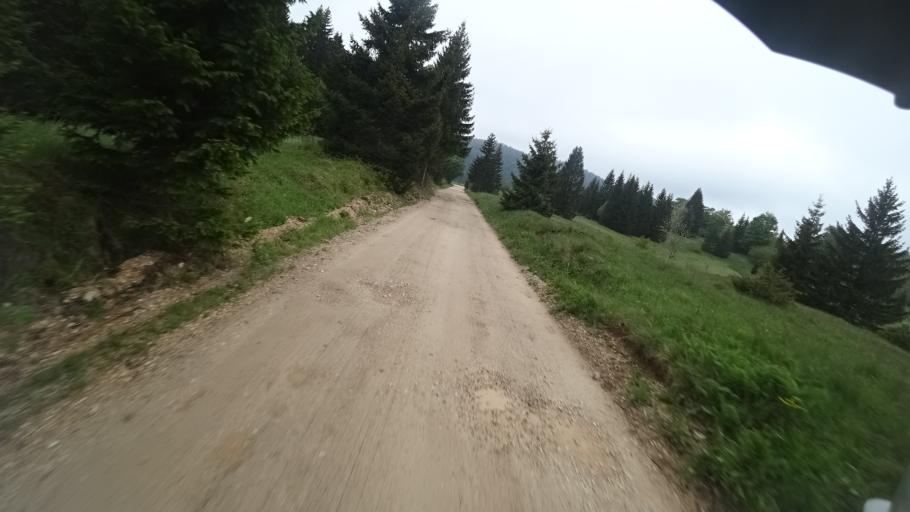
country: BA
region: Federation of Bosnia and Herzegovina
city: Bihac
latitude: 44.6456
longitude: 15.8541
